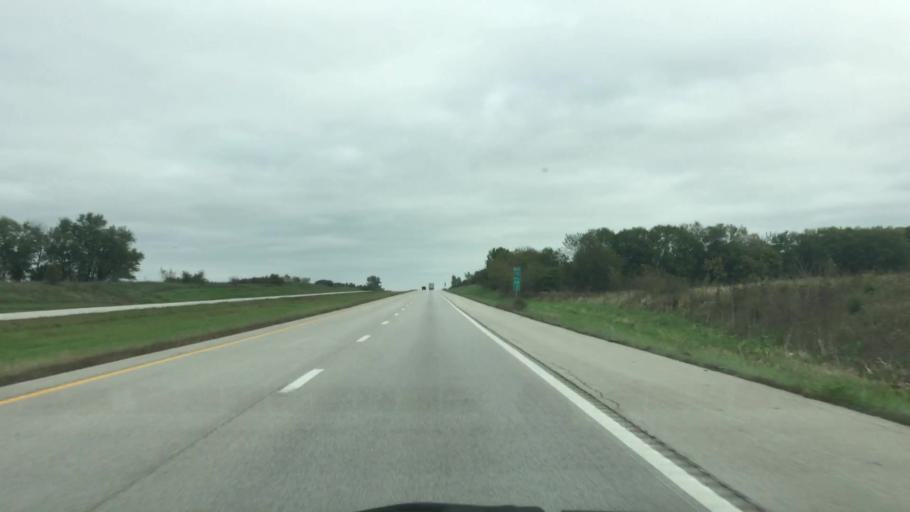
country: US
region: Missouri
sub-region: Clinton County
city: Cameron
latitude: 39.8053
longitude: -94.1980
